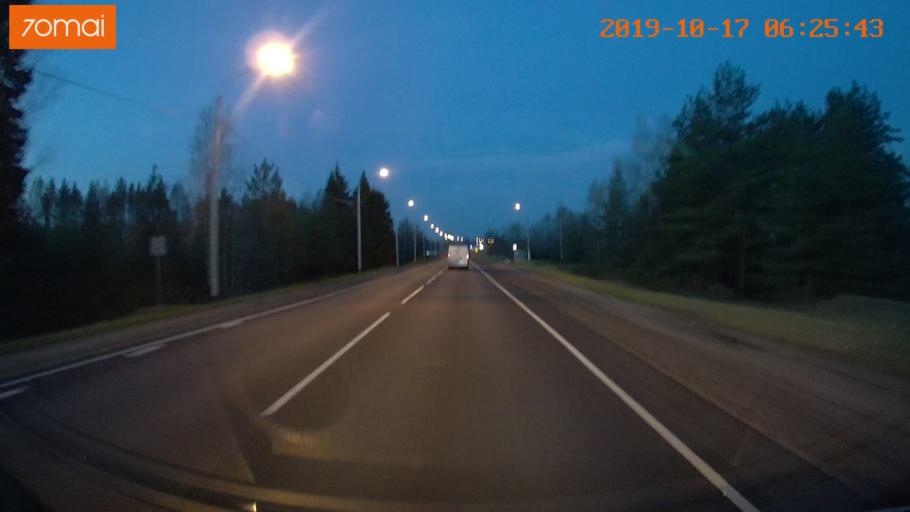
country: RU
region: Ivanovo
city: Lezhnevo
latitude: 56.7666
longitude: 40.8017
